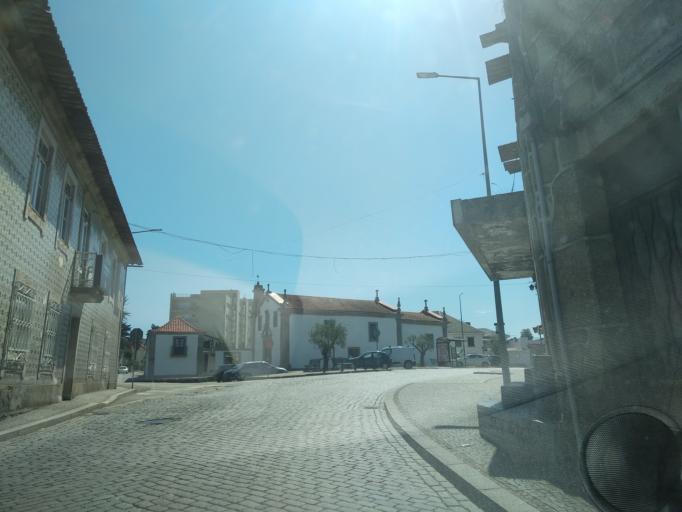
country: PT
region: Porto
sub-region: Pacos de Ferreira
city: Freamunde
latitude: 41.2888
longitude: -8.3382
